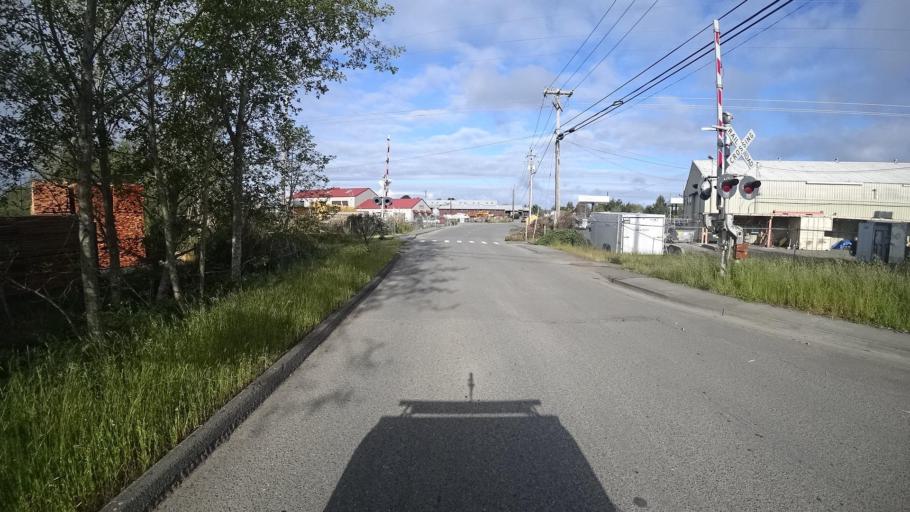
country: US
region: California
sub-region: Humboldt County
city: Arcata
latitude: 40.9012
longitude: -124.0727
